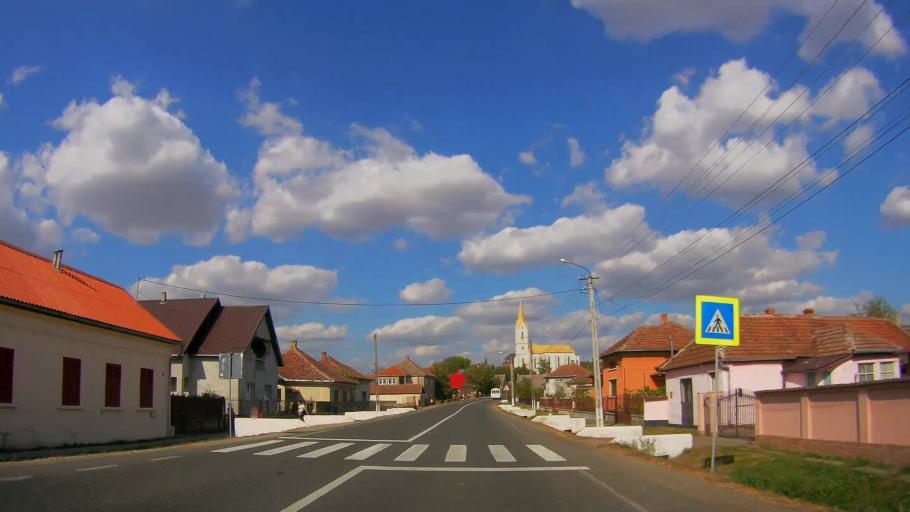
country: RO
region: Satu Mare
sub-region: Oras Ardud
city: Ardud
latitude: 47.6357
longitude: 22.8849
